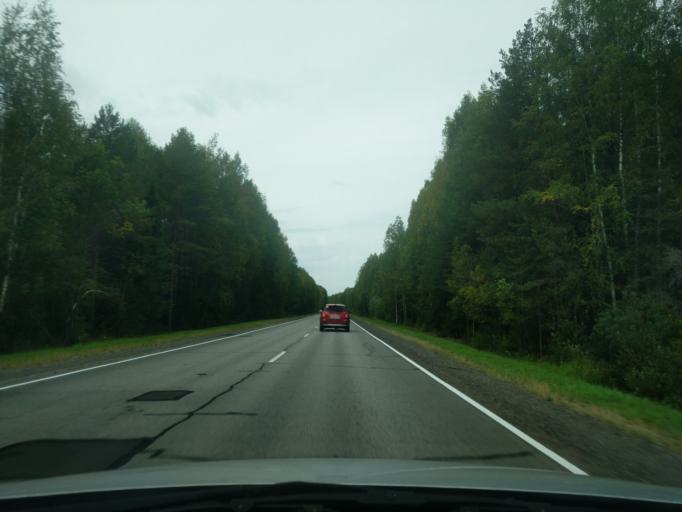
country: RU
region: Kirov
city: Kotel'nich
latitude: 58.2711
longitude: 48.0874
